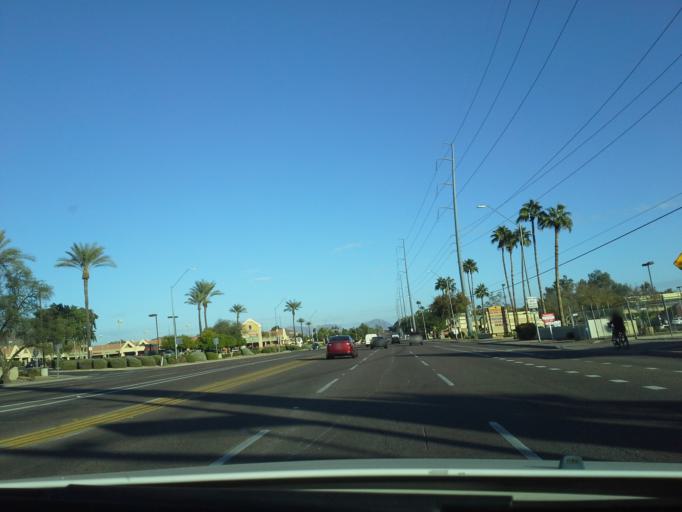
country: US
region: Arizona
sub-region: Maricopa County
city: Glendale
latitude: 33.6548
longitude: -112.0653
